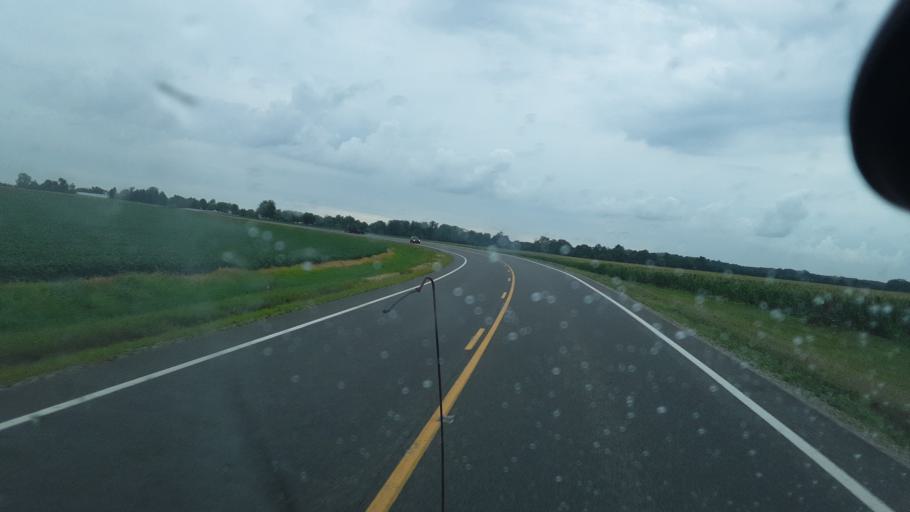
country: US
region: Ohio
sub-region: Williams County
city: Bryan
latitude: 41.4191
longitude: -84.6157
